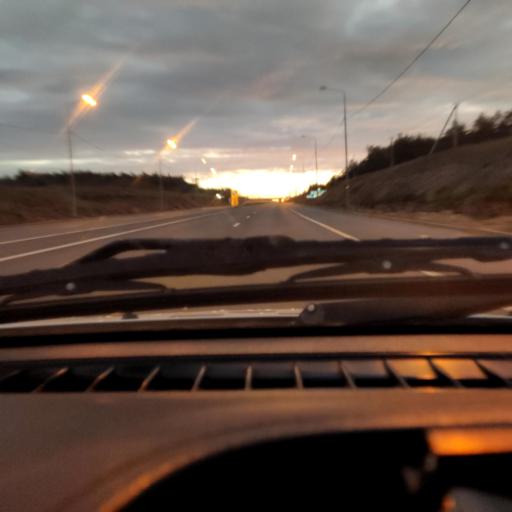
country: RU
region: Samara
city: Zhigulevsk
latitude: 53.4933
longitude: 49.5272
